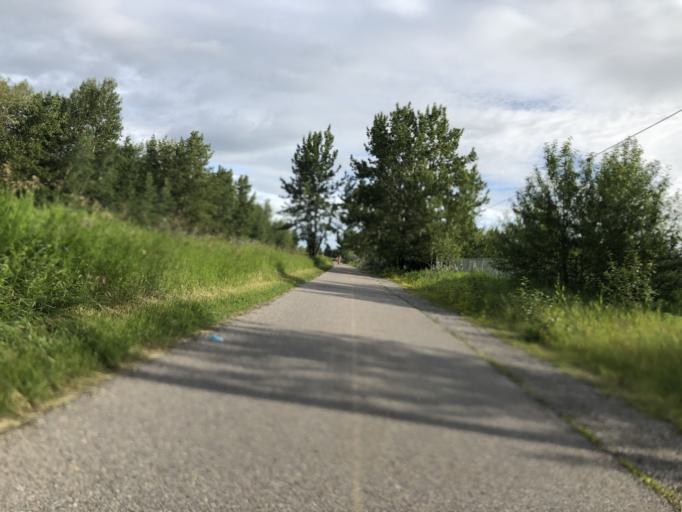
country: CA
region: Alberta
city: Calgary
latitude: 51.0240
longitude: -114.0115
